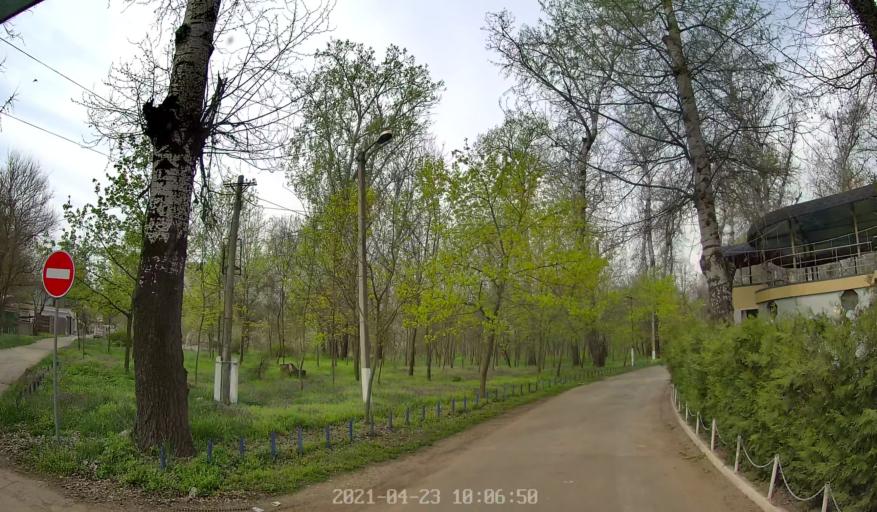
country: MD
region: Chisinau
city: Vadul lui Voda
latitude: 47.0847
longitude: 29.1121
